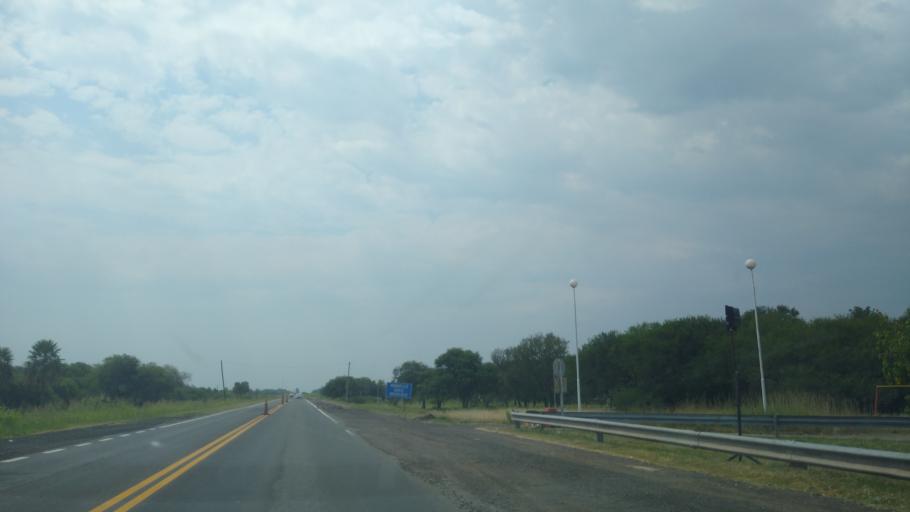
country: AR
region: Chaco
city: Margarita Belen
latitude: -27.1174
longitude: -58.9704
